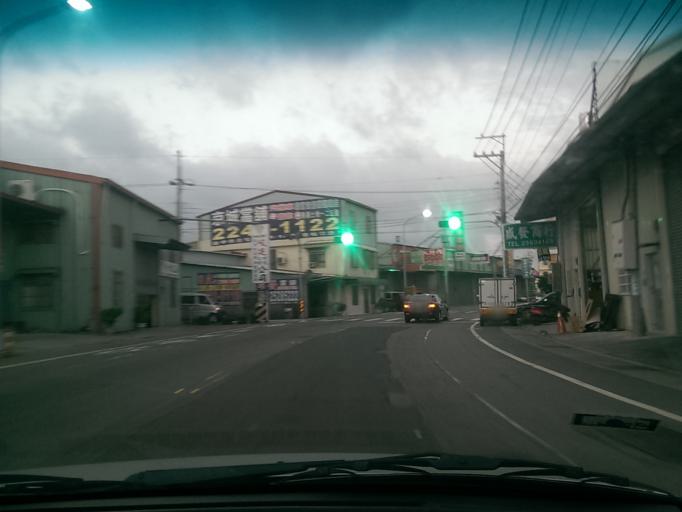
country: TW
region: Taiwan
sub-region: Taichung City
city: Taichung
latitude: 24.2168
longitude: 120.6363
